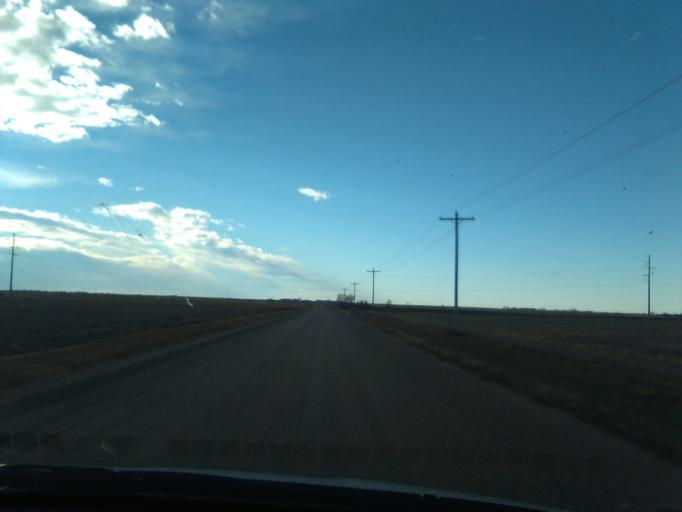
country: US
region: Nebraska
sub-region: Kearney County
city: Minden
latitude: 40.3649
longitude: -98.8707
